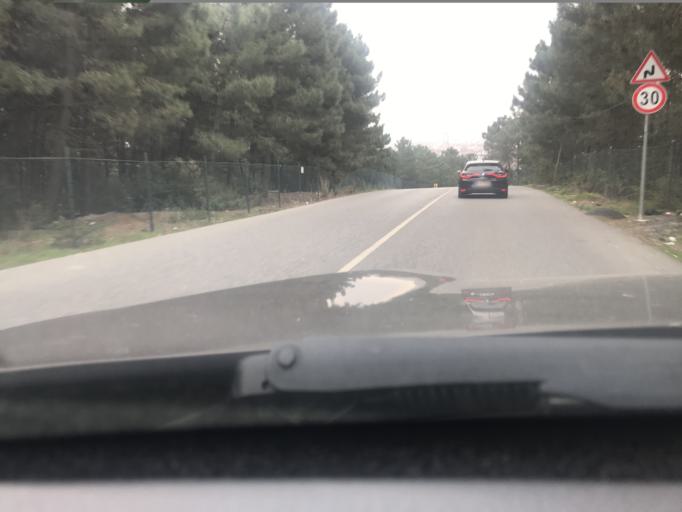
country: TR
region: Istanbul
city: Umraniye
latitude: 41.0423
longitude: 29.1705
